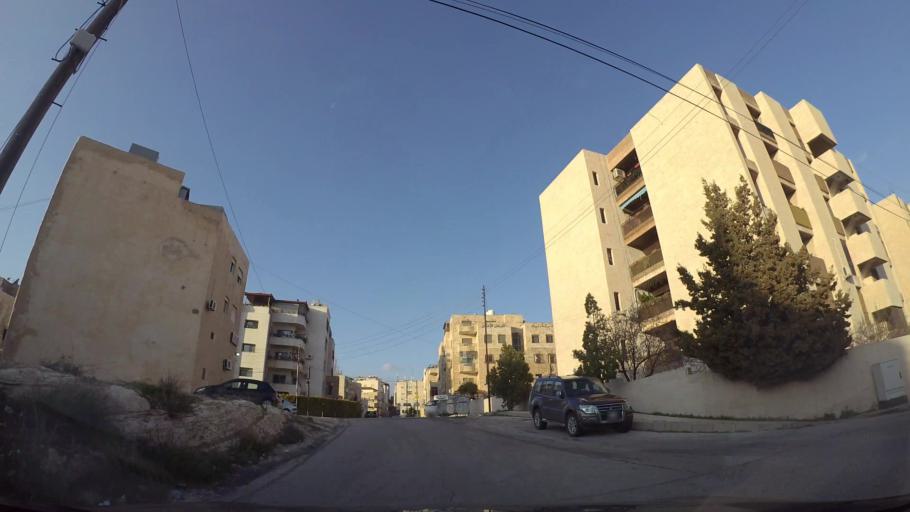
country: JO
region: Amman
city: Al Jubayhah
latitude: 31.9778
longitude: 35.8676
